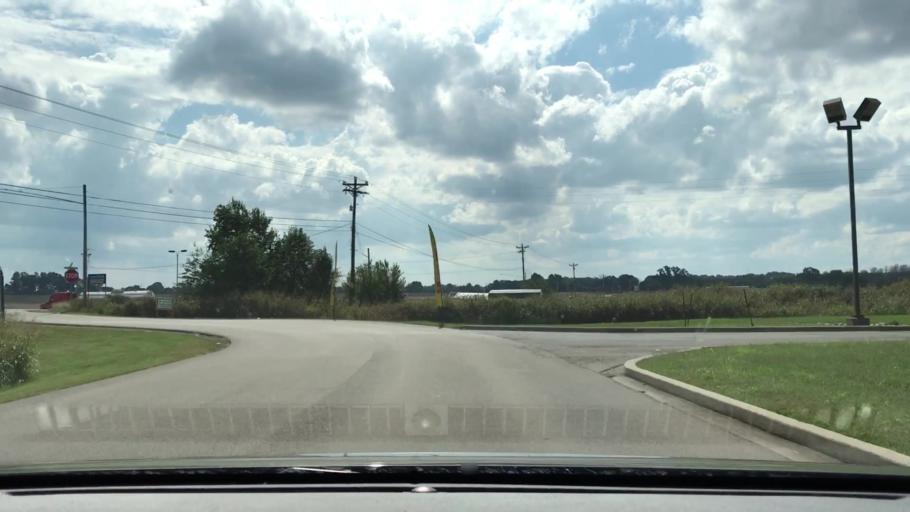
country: US
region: Kentucky
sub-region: Christian County
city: Oak Grove
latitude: 36.6791
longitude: -87.4062
